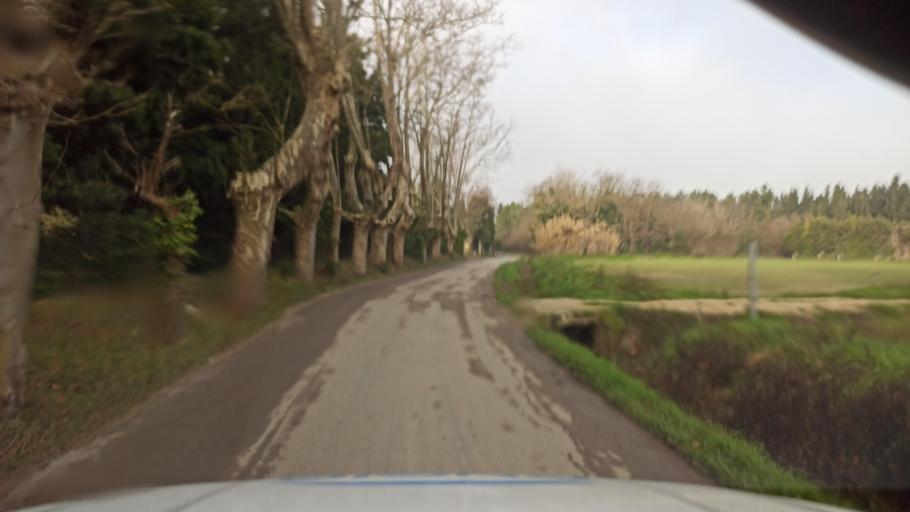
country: FR
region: Provence-Alpes-Cote d'Azur
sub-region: Departement des Bouches-du-Rhone
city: Rognonas
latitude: 43.8934
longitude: 4.7934
